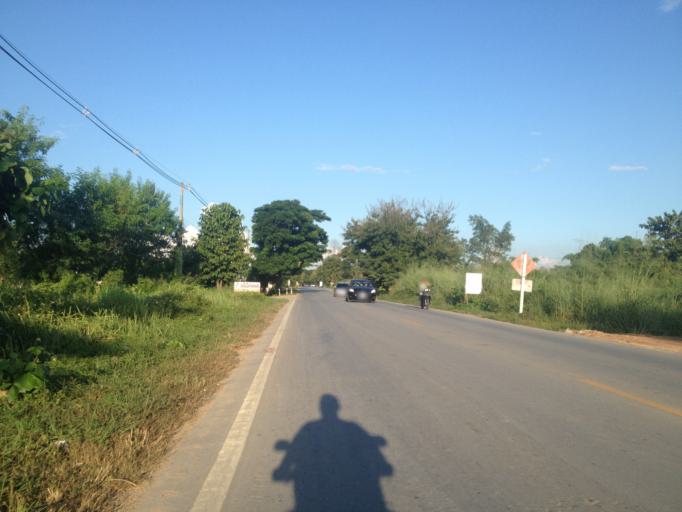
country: TH
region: Chiang Mai
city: San Pa Tong
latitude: 18.6141
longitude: 98.8576
